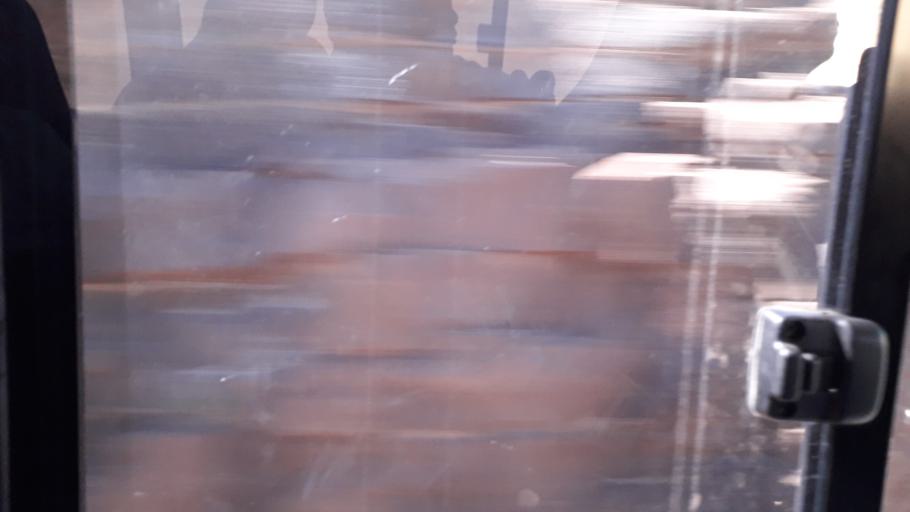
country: LS
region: Mokhotlong
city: Mokhotlong
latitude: -29.2779
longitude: 28.9336
